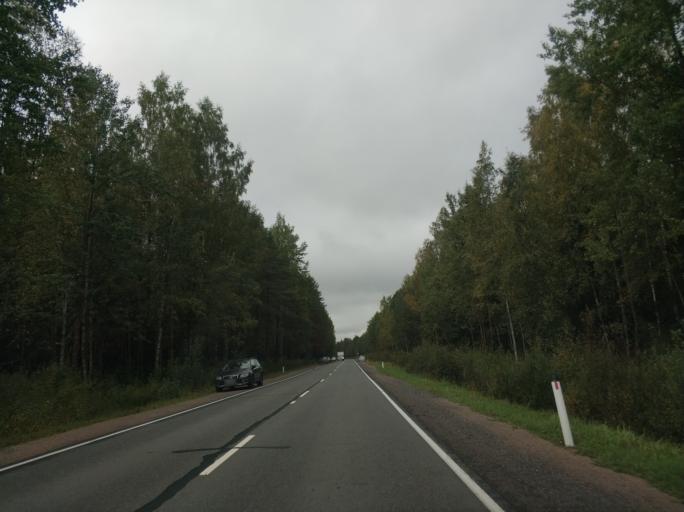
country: RU
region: Leningrad
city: Shcheglovo
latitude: 60.1014
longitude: 30.8282
